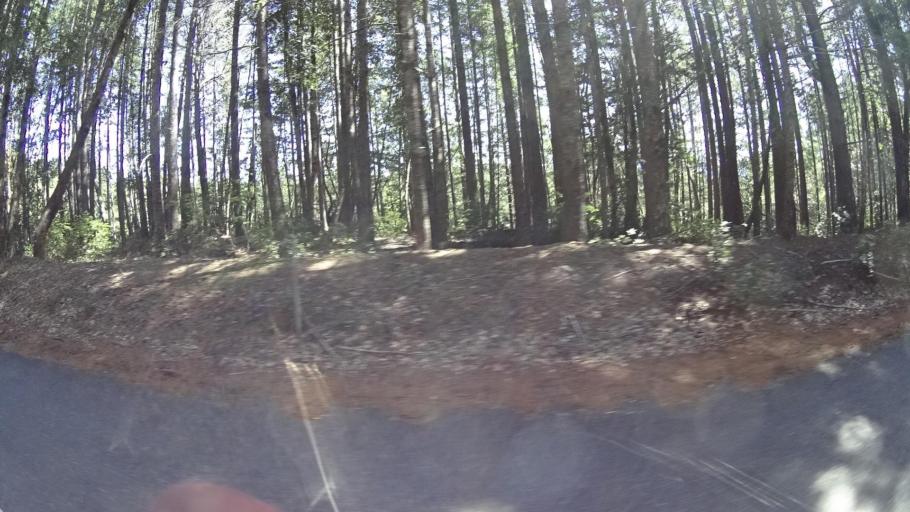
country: US
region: California
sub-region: Humboldt County
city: Redway
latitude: 40.1953
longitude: -124.0959
